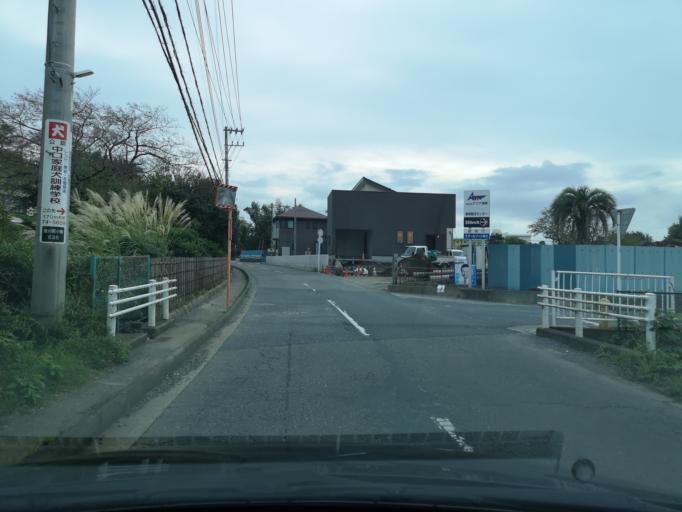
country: JP
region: Kanagawa
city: Chigasaki
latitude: 35.3850
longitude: 139.3967
